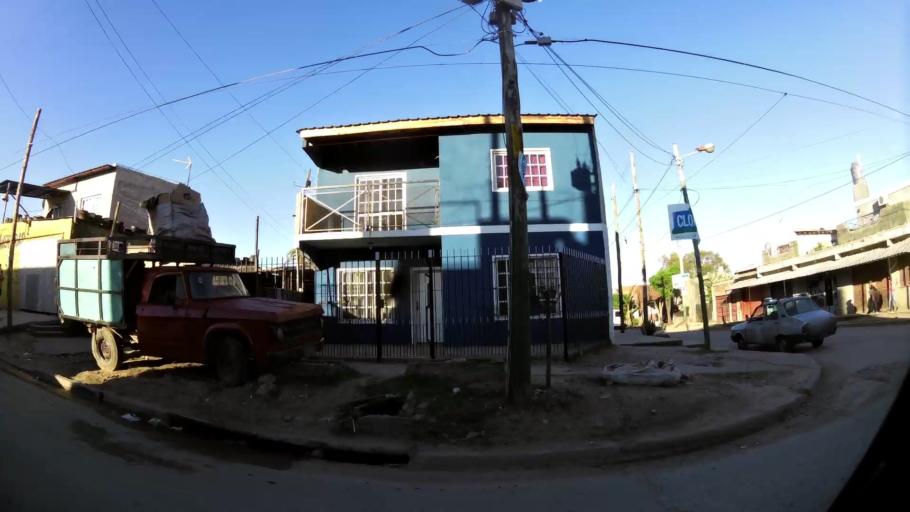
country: AR
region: Buenos Aires
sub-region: Partido de Almirante Brown
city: Adrogue
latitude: -34.7717
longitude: -58.3371
